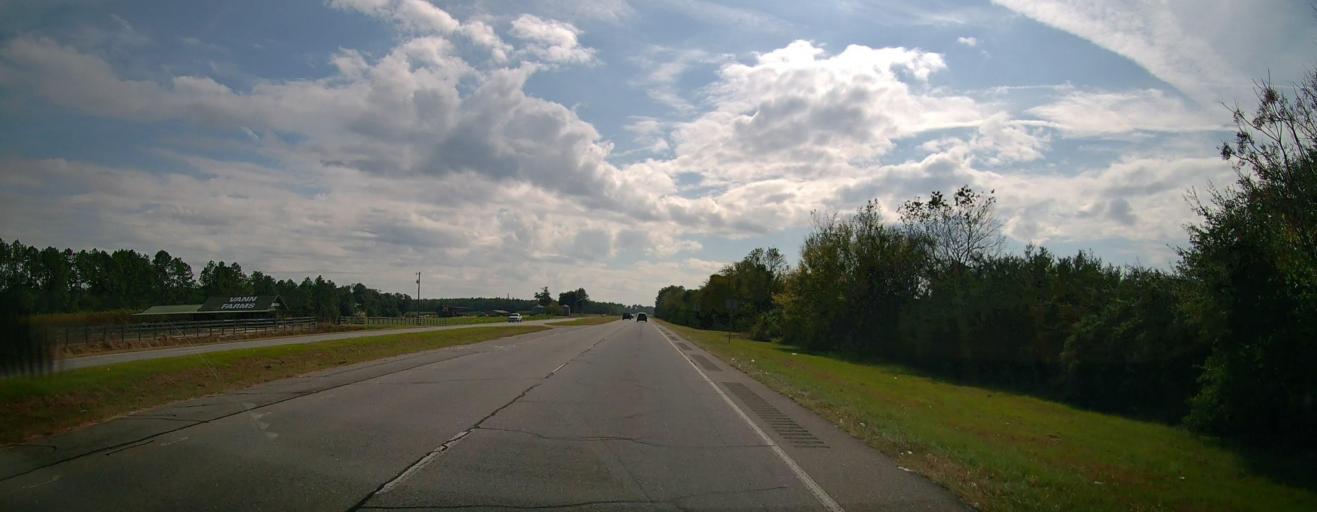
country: US
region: Georgia
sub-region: Mitchell County
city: Camilla
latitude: 31.3309
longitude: -84.1719
